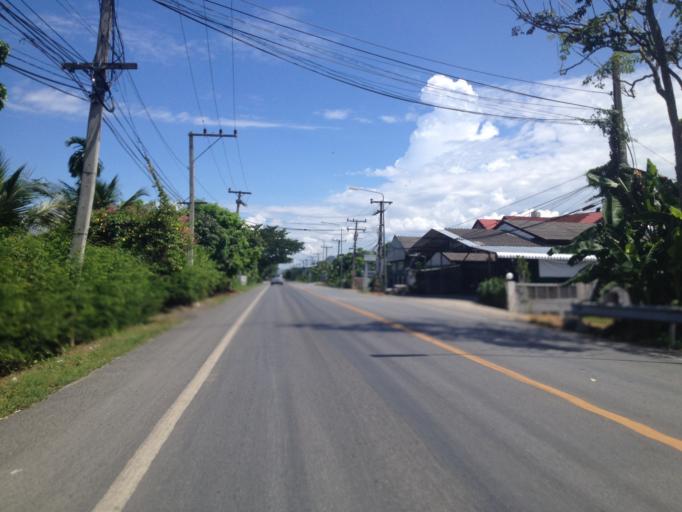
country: TH
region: Lamphun
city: Lamphun
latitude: 18.6031
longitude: 98.9597
